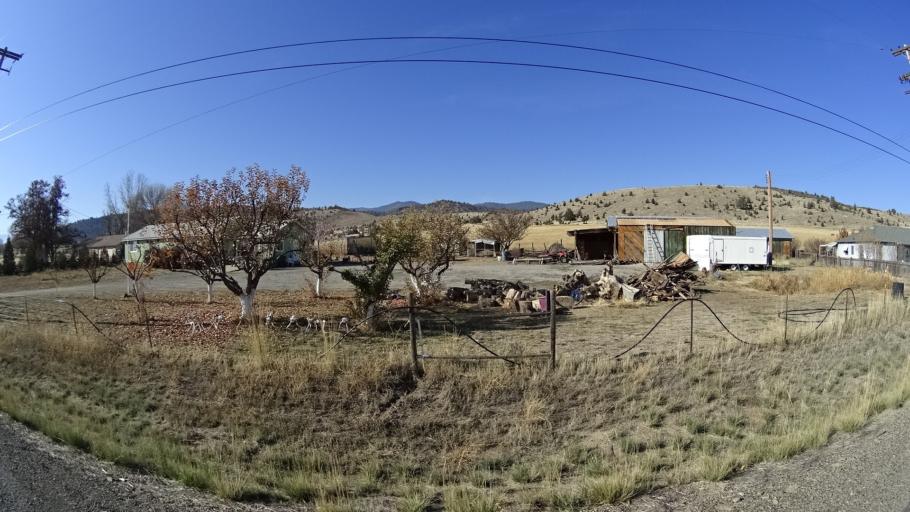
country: US
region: California
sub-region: Siskiyou County
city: Montague
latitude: 41.6375
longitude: -122.5320
